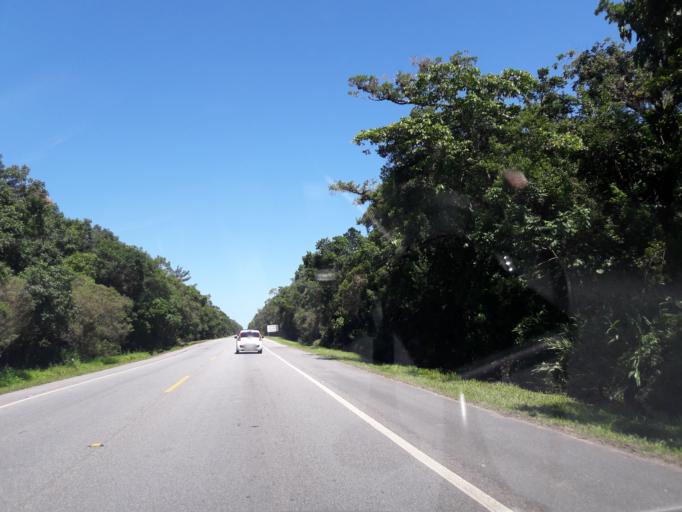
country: BR
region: Parana
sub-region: Pontal Do Parana
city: Pontal do Parana
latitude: -25.6490
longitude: -48.5283
